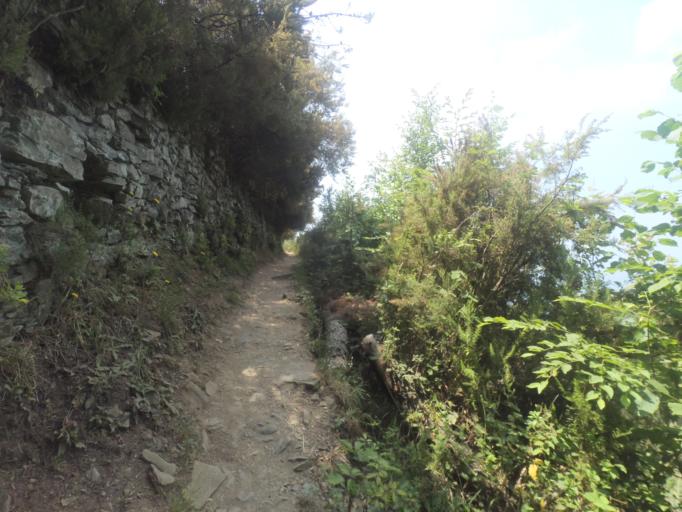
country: IT
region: Liguria
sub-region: Provincia di La Spezia
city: Riomaggiore
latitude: 44.1224
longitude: 9.7228
